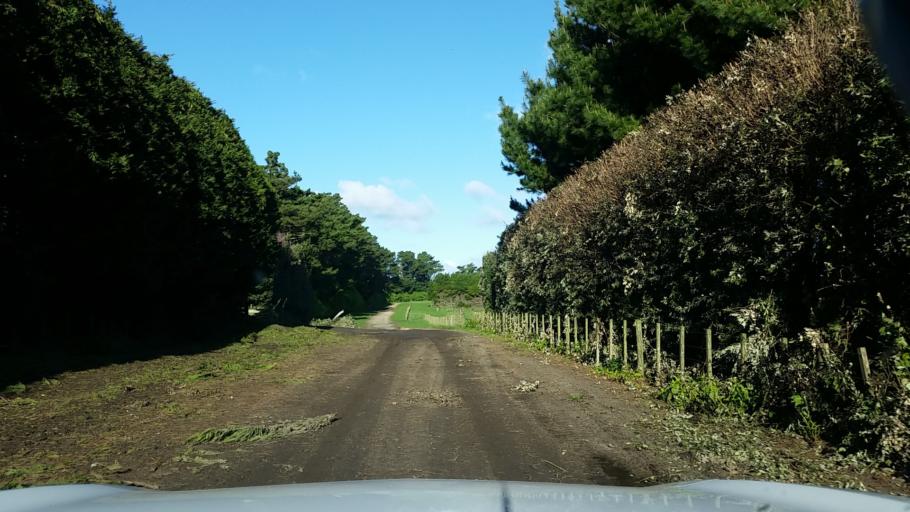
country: NZ
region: Taranaki
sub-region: South Taranaki District
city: Patea
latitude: -39.7379
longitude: 174.5413
